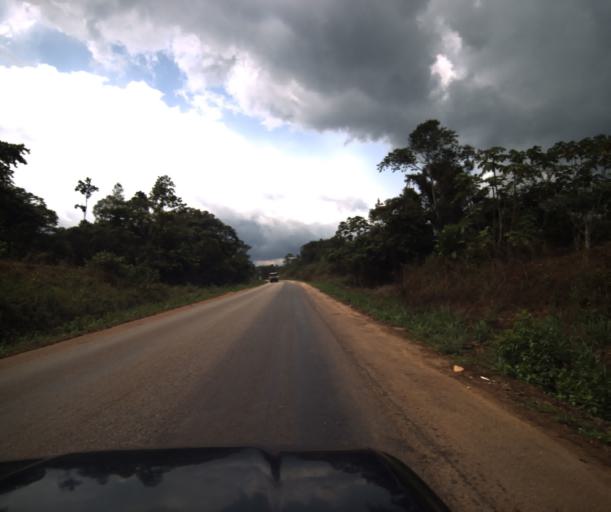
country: CM
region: Littoral
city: Edea
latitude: 3.9335
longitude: 10.0541
